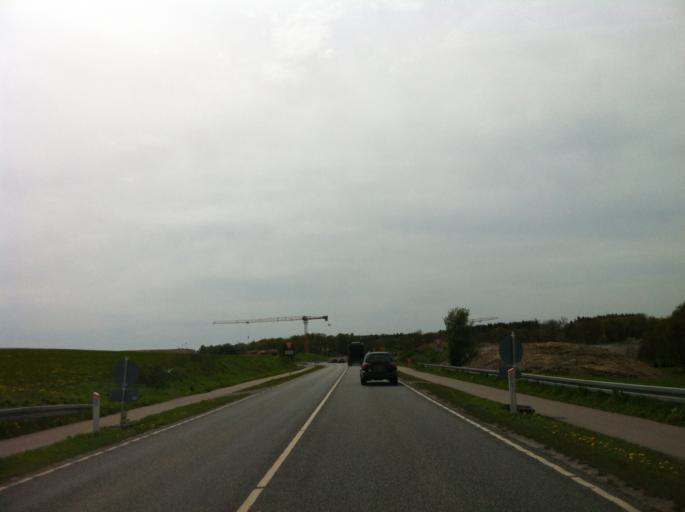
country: DK
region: Zealand
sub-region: Naestved Kommune
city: Naestved
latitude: 55.2664
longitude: 11.7552
